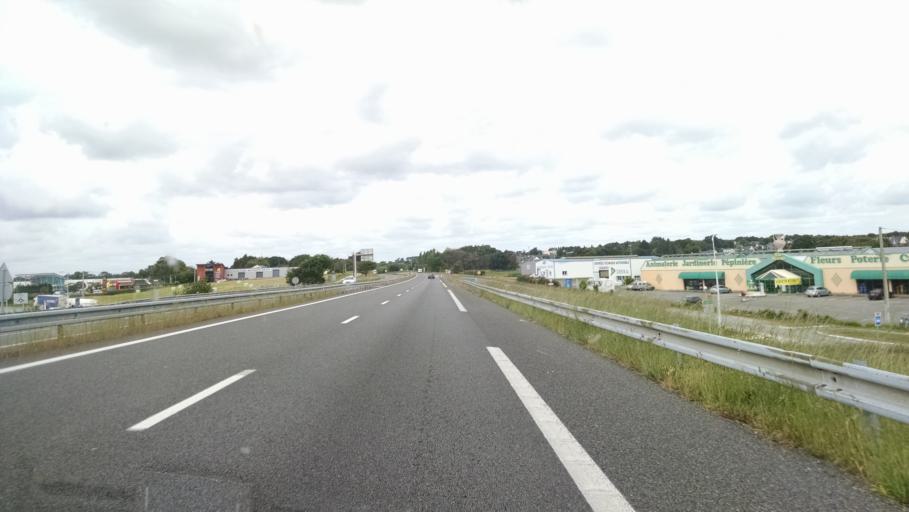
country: FR
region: Brittany
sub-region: Departement du Morbihan
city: Muzillac
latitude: 47.5588
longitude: -2.4998
